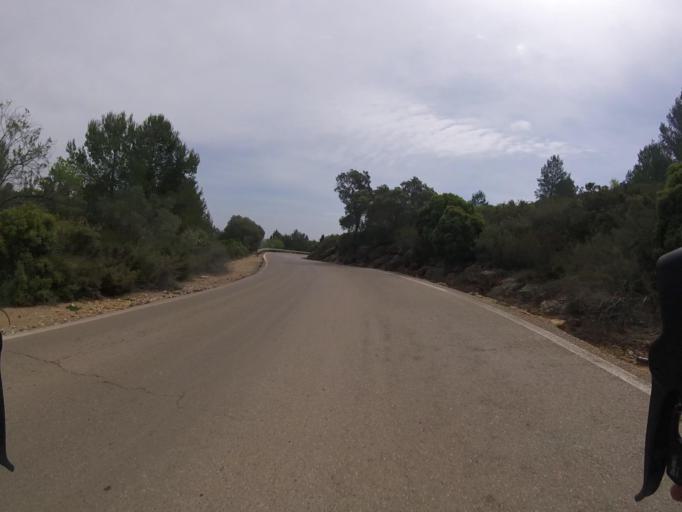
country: ES
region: Valencia
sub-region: Provincia de Castello
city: Cabanes
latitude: 40.1602
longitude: 0.0773
